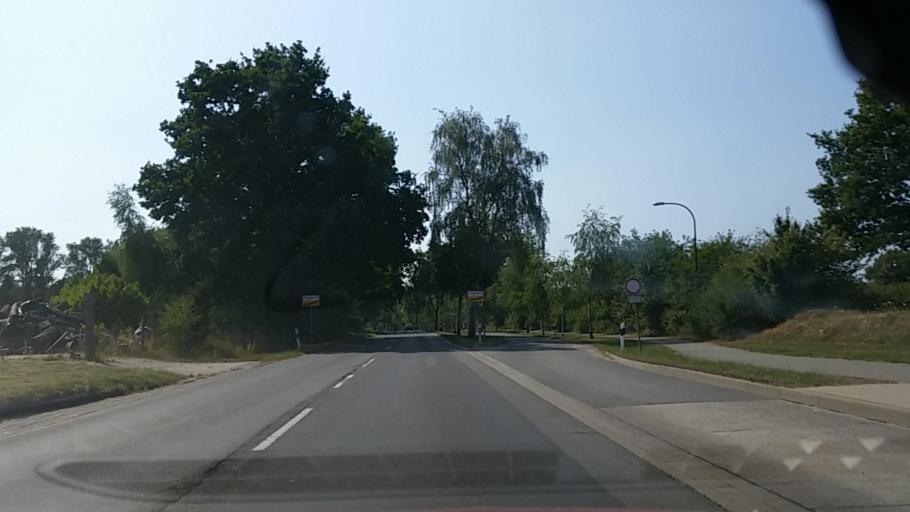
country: DE
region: Schleswig-Holstein
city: Glinde
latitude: 53.5415
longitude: 10.1870
